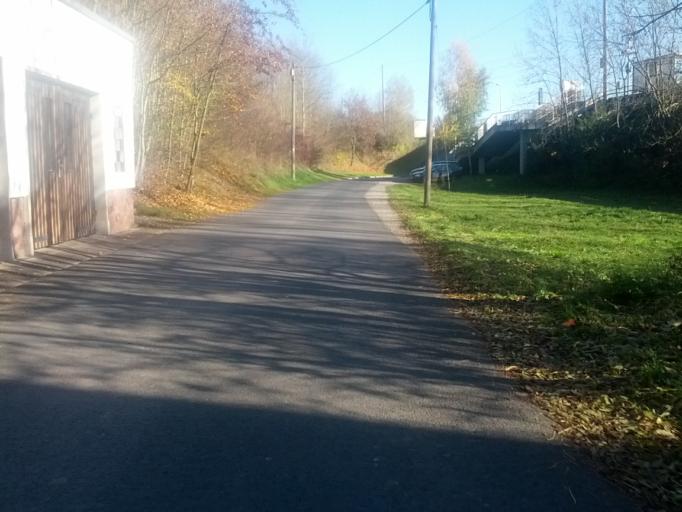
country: DE
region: Thuringia
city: Mechterstadt
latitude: 50.9464
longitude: 10.4801
